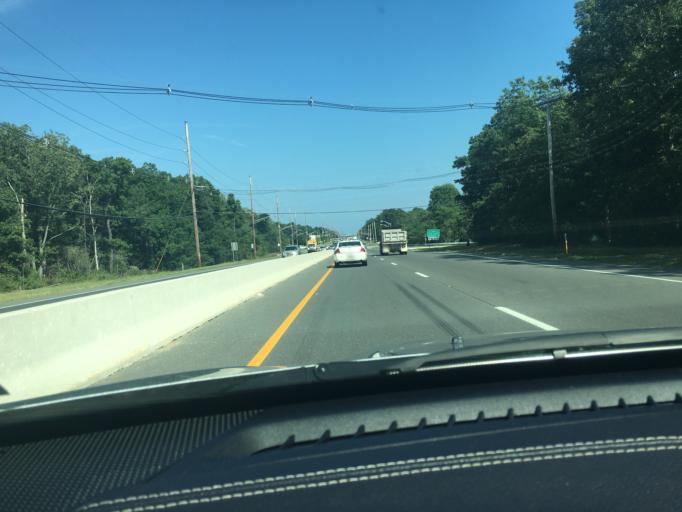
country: US
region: New Jersey
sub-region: Ocean County
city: Leisure Village
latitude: 40.0512
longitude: -74.1913
